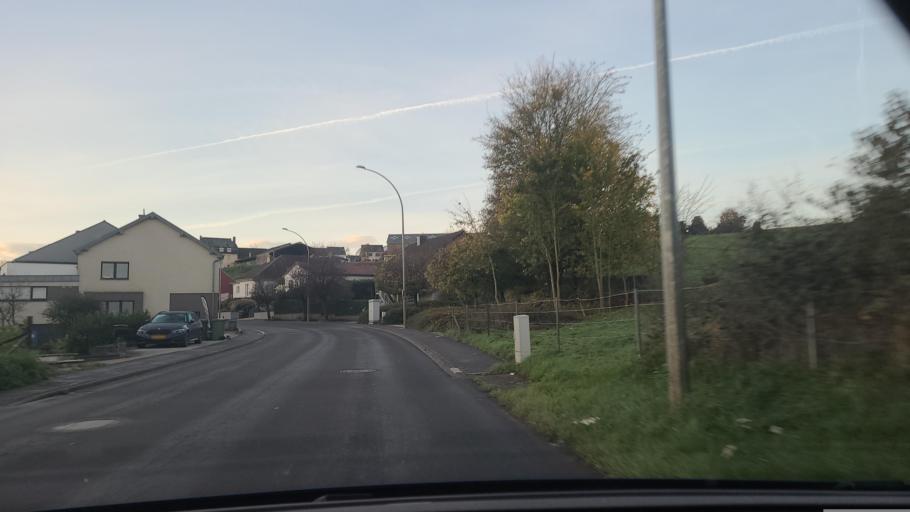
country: LU
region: Luxembourg
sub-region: Canton de Capellen
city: Garnich
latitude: 49.6044
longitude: 5.9476
